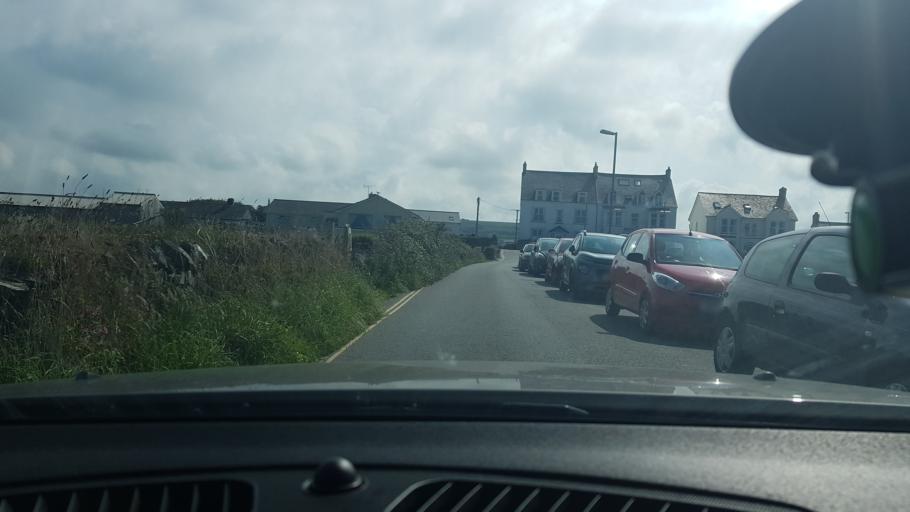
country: GB
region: England
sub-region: Cornwall
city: Tintagel
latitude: 50.6670
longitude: -4.7528
